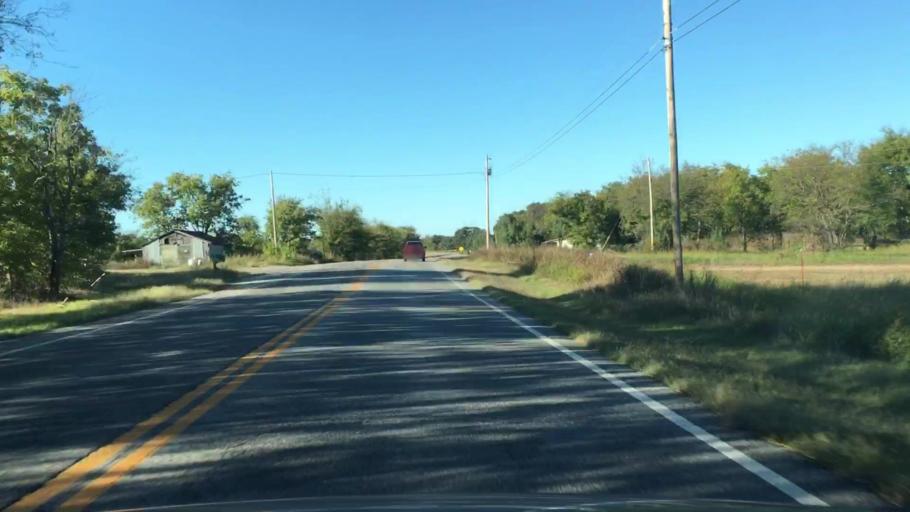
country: US
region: Oklahoma
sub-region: Cherokee County
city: Tahlequah
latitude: 35.9253
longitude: -95.1238
